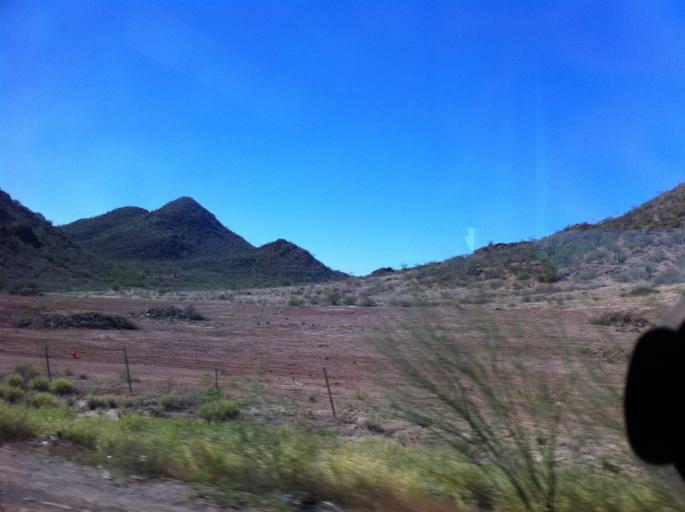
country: MX
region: Sonora
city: Heroica Guaymas
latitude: 27.9754
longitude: -110.9383
